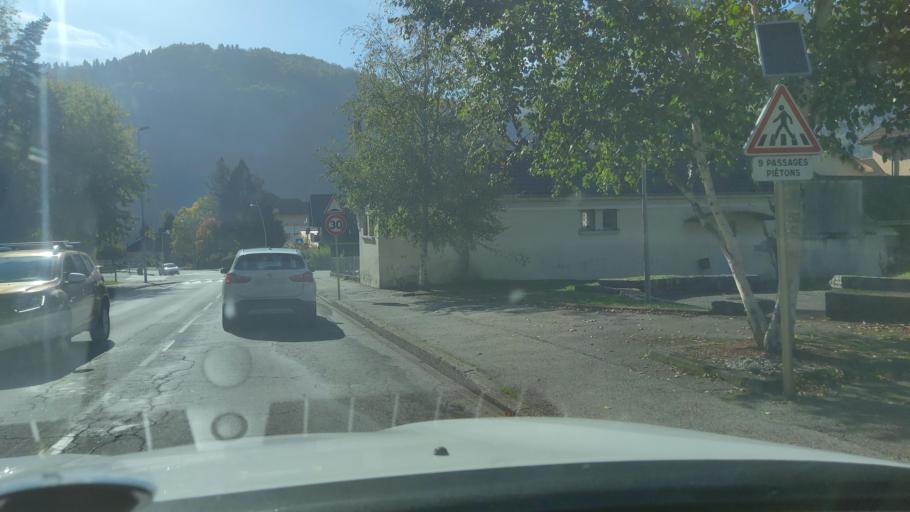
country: FR
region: Rhone-Alpes
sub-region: Departement de la Savoie
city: Ugine
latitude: 45.7525
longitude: 6.4180
